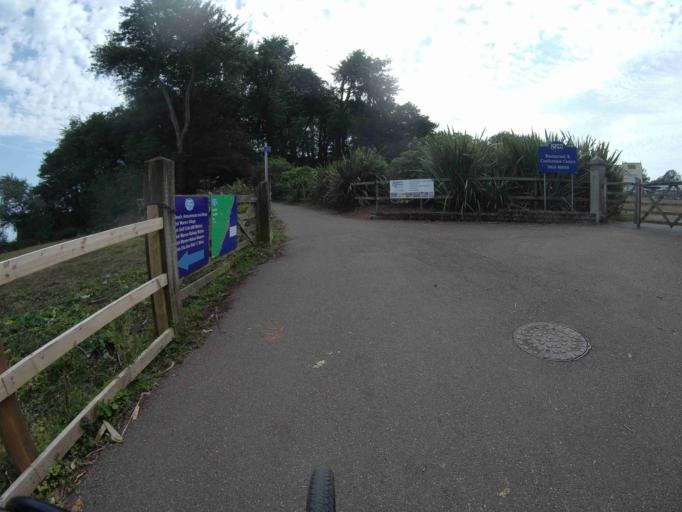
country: GB
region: England
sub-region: Devon
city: Dawlish
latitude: 50.5941
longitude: -3.4448
